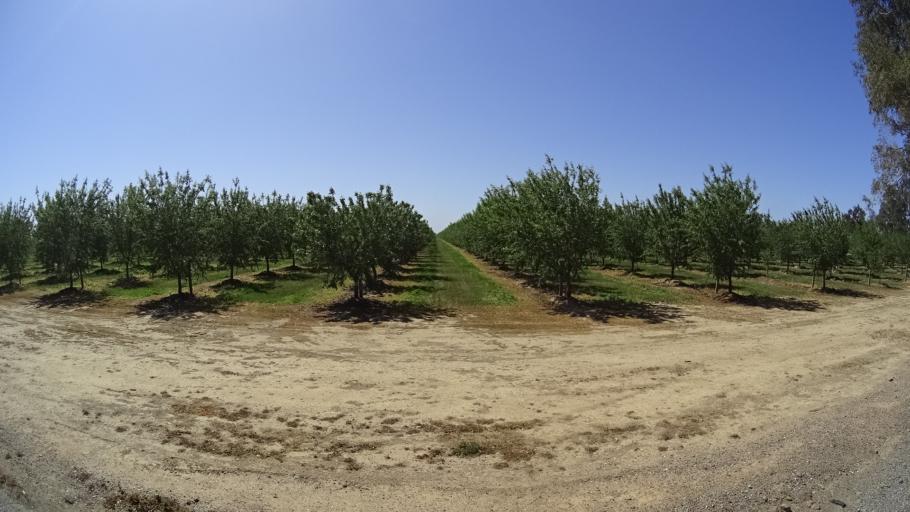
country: US
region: California
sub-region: Glenn County
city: Orland
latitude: 39.6967
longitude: -122.1860
